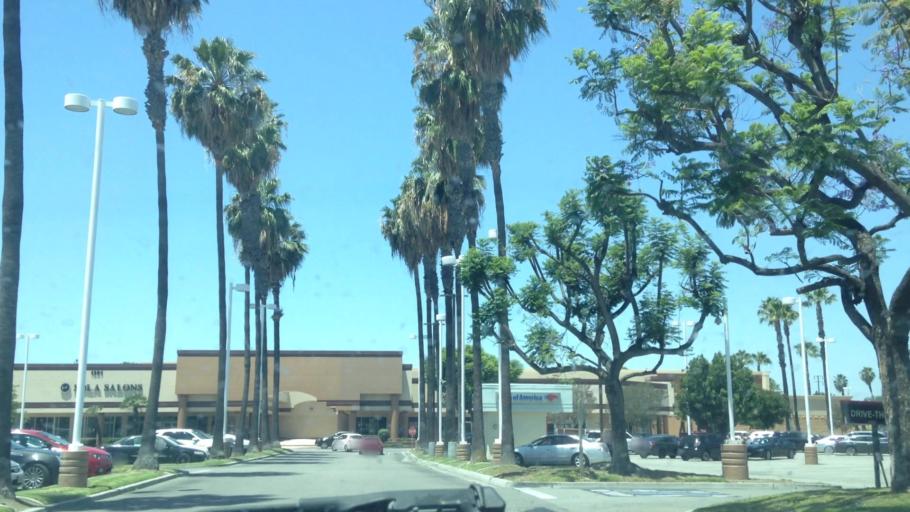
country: US
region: California
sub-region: Orange County
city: Fullerton
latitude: 33.8580
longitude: -117.9249
